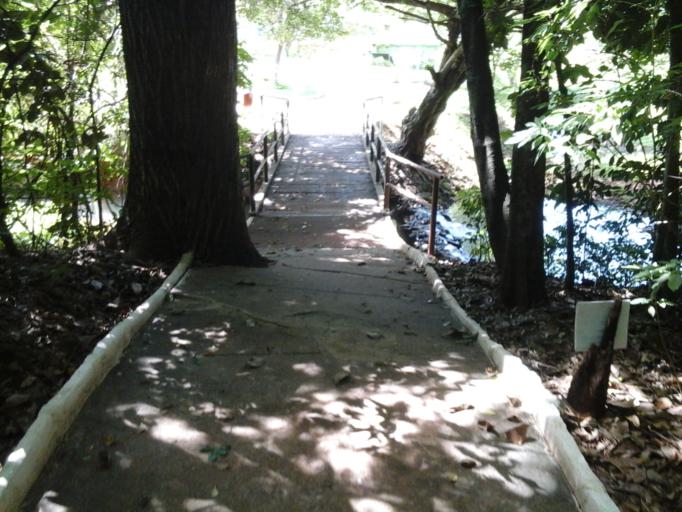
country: BR
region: Minas Gerais
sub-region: Patos De Minas
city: Patos de Minas
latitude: -18.5830
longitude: -46.5047
